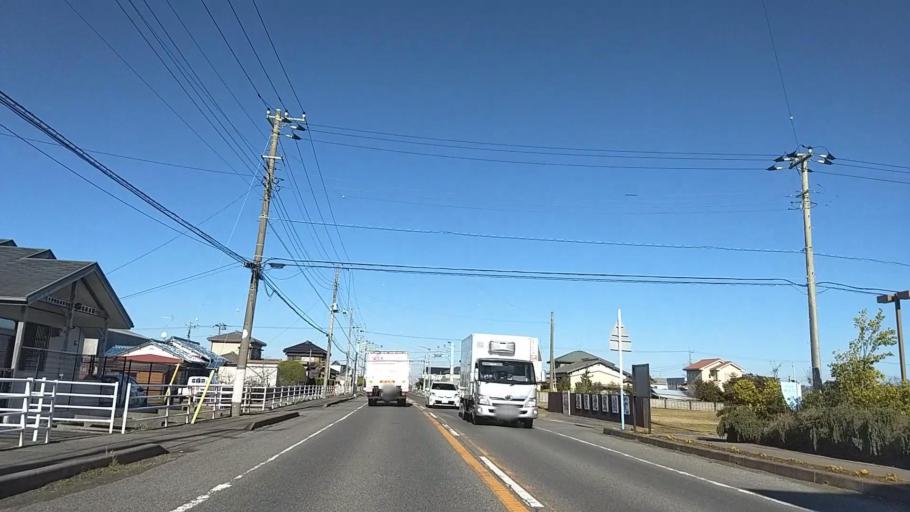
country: JP
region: Chiba
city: Togane
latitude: 35.5018
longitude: 140.4291
